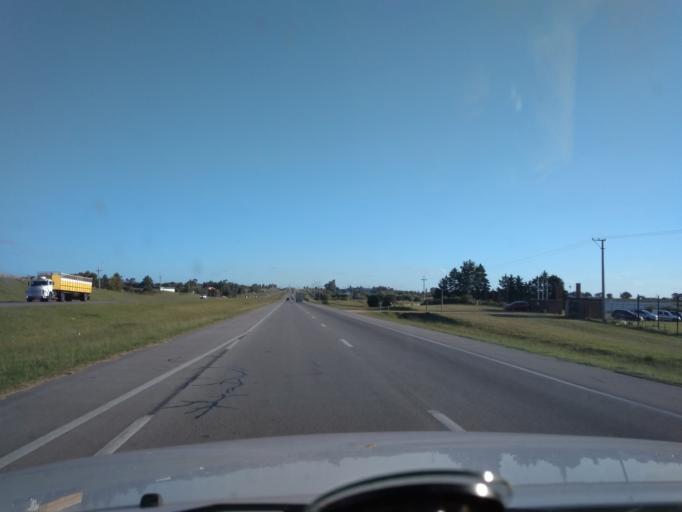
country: UY
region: Canelones
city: Las Piedras
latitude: -34.7057
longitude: -56.2414
